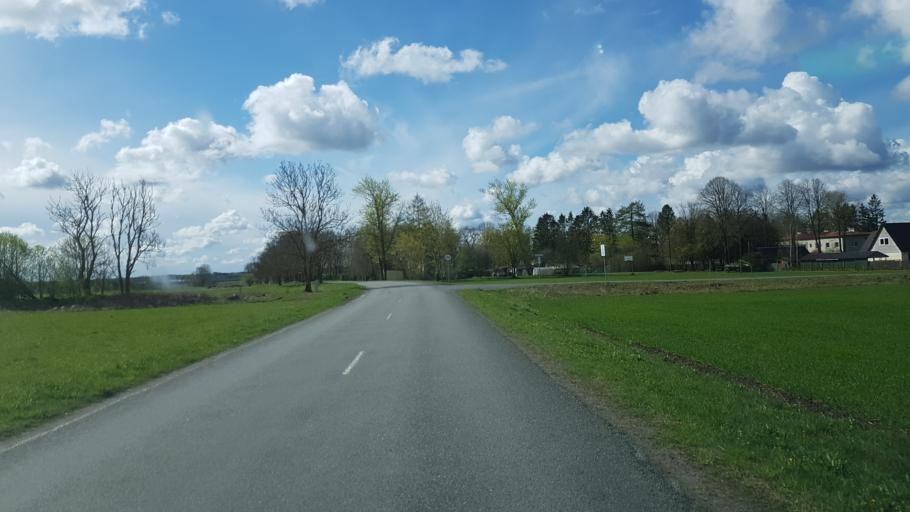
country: EE
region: Harju
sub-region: Kiili vald
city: Kiili
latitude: 59.2767
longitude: 24.8746
